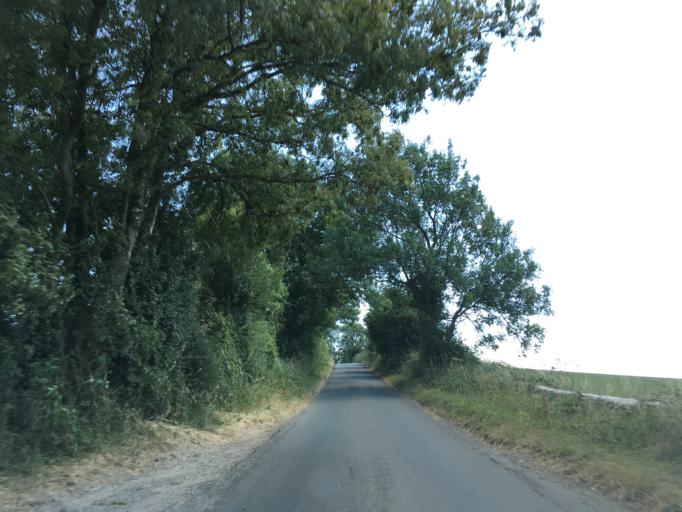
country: GB
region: England
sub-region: Gloucestershire
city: Chalford
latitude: 51.7030
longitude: -2.1090
